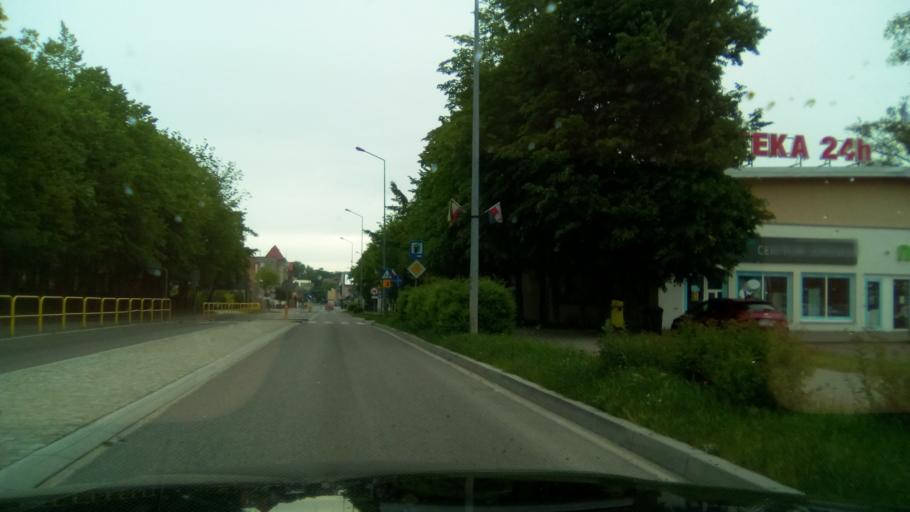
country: PL
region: Pomeranian Voivodeship
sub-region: Powiat chojnicki
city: Chojnice
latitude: 53.6944
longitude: 17.5571
